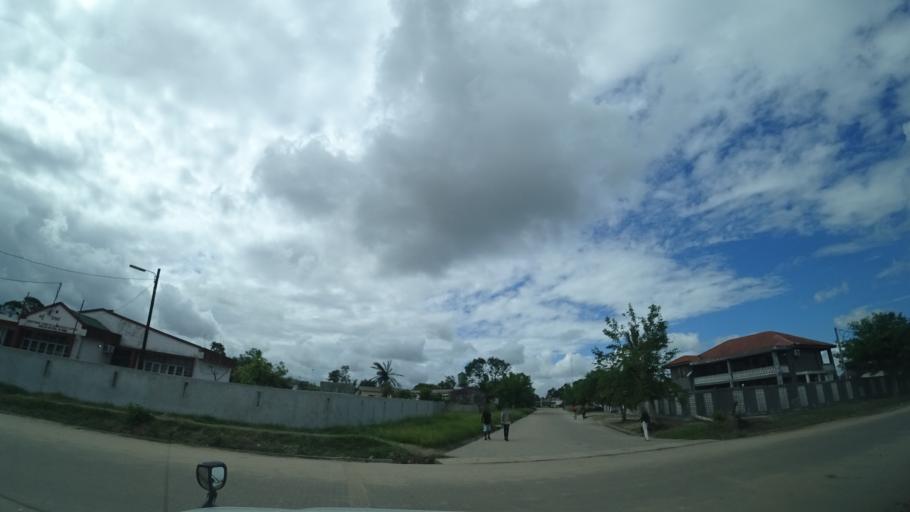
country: MZ
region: Sofala
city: Dondo
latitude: -19.6171
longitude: 34.7444
